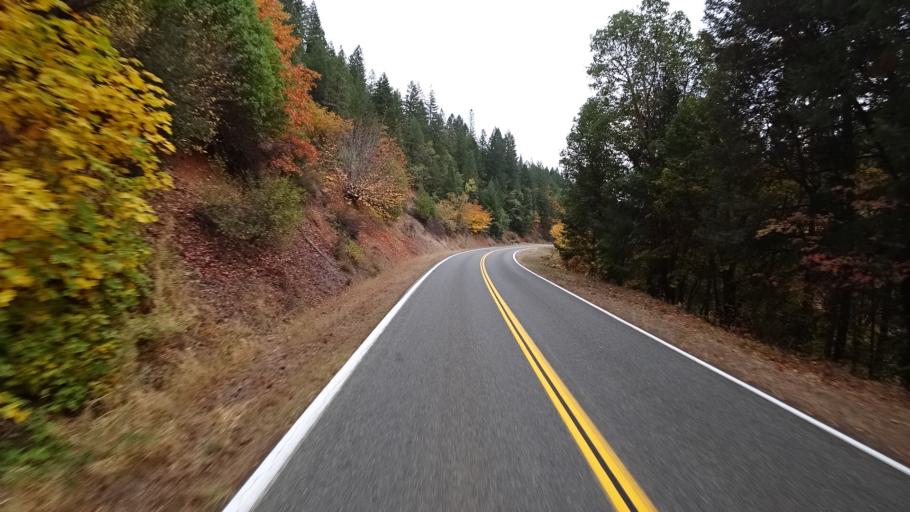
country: US
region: California
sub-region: Siskiyou County
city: Happy Camp
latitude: 41.9060
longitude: -123.4417
